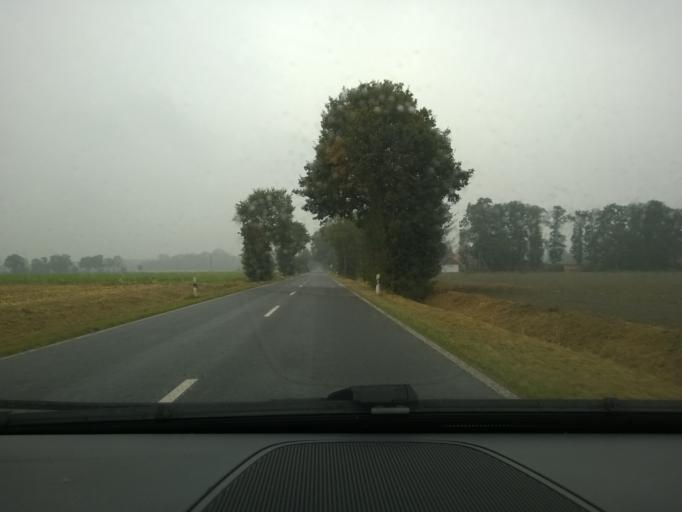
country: DE
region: North Rhine-Westphalia
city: Stadtlohn
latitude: 51.9492
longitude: 6.9432
